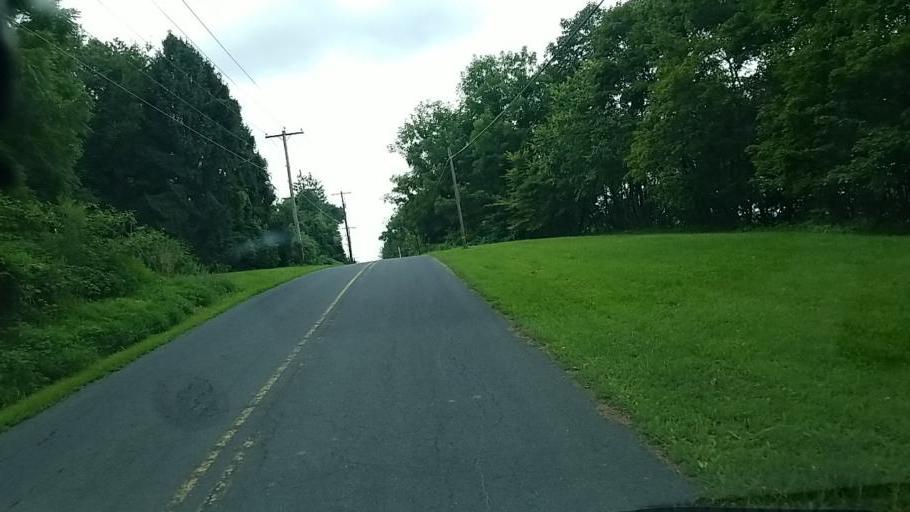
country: US
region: Pennsylvania
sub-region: Dauphin County
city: Elizabethville
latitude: 40.6563
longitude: -76.8602
